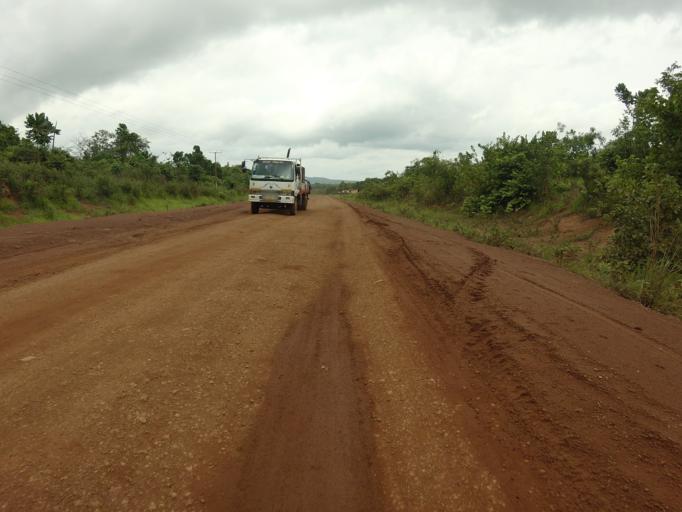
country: GH
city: Kpandae
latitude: 8.3014
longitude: 0.4860
